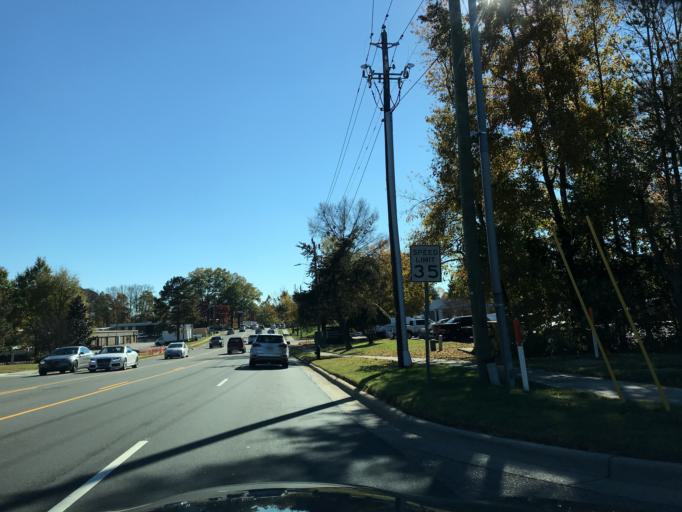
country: US
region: North Carolina
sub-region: Wake County
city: Raleigh
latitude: 35.8419
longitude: -78.6014
